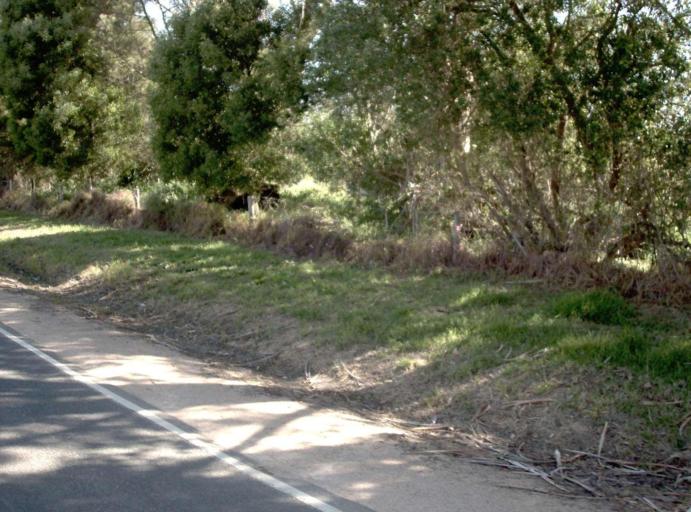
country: AU
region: Victoria
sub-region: East Gippsland
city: Lakes Entrance
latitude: -37.7288
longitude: 148.5038
